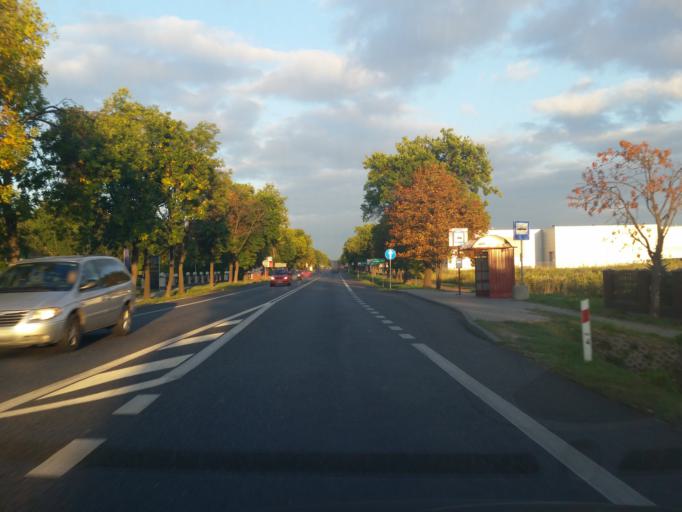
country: PL
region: Masovian Voivodeship
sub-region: Powiat warszawski zachodni
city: Jozefow
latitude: 52.2118
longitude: 20.7412
